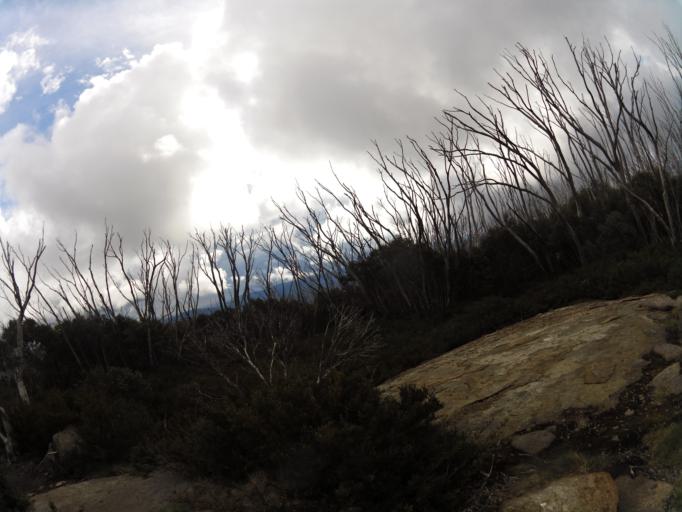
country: AU
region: Victoria
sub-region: Yarra Ranges
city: Millgrove
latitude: -37.5032
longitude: 145.8799
